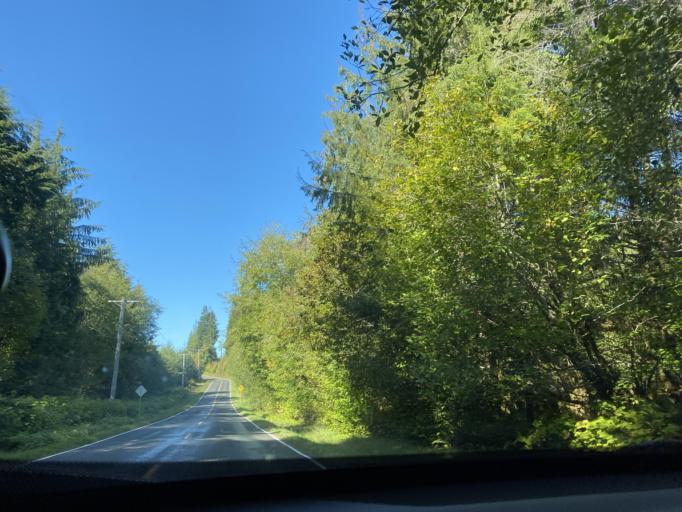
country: US
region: Washington
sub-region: Clallam County
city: Forks
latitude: 47.9481
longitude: -124.5031
